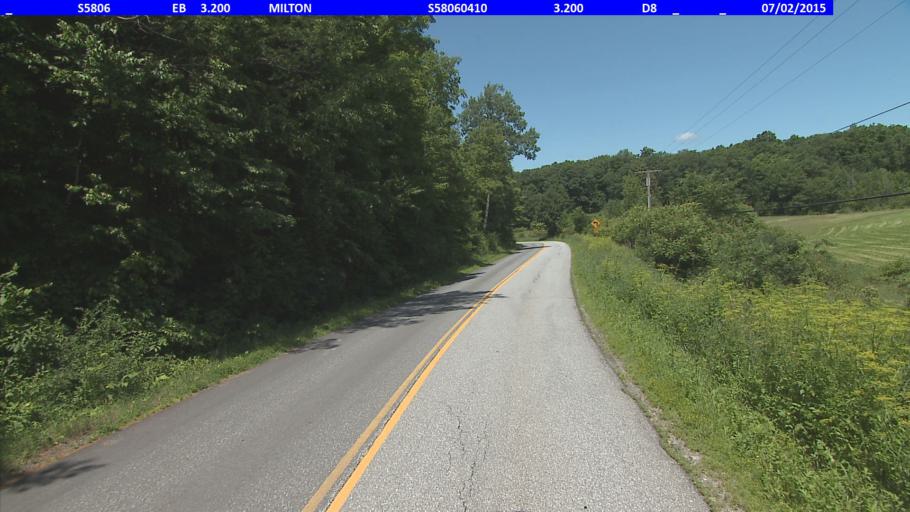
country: US
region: Vermont
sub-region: Chittenden County
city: Milton
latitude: 44.6699
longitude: -73.1704
